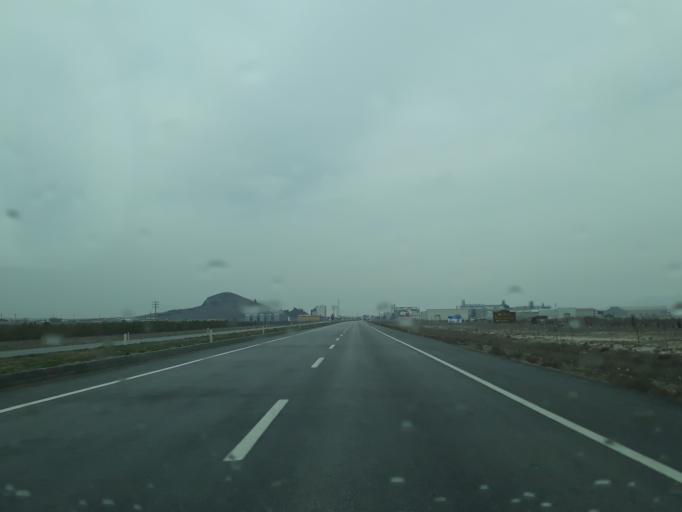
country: TR
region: Konya
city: Karapinar
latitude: 37.7131
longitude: 33.5999
